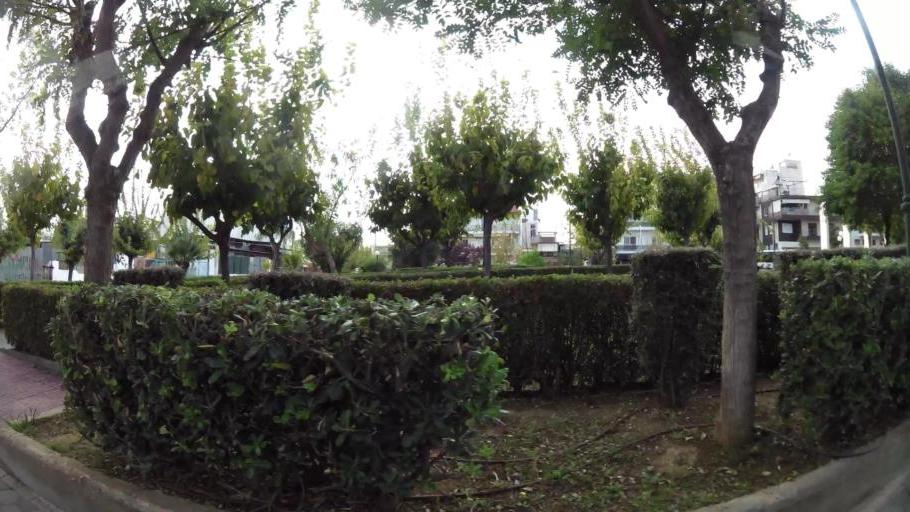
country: GR
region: Attica
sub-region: Nomarchia Athinas
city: Ilion
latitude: 38.0438
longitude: 23.7015
